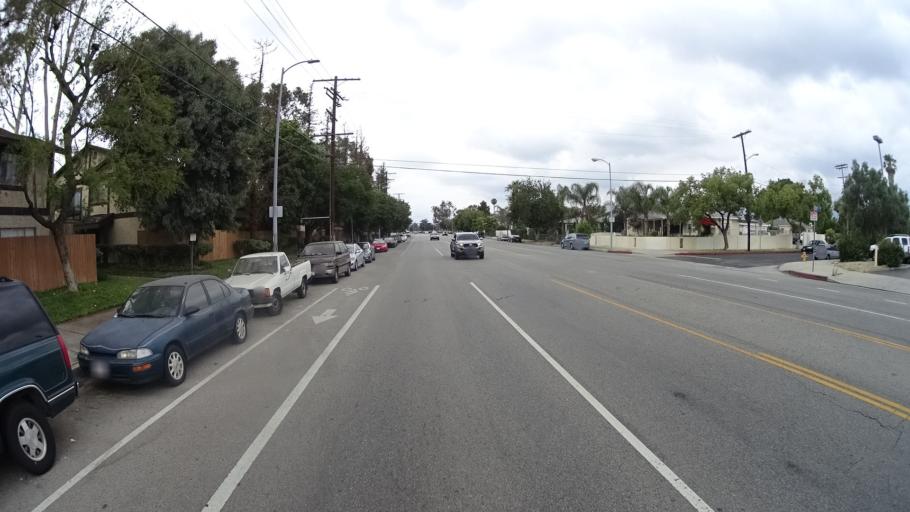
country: US
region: California
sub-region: Los Angeles County
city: San Fernando
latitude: 34.2484
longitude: -118.4486
